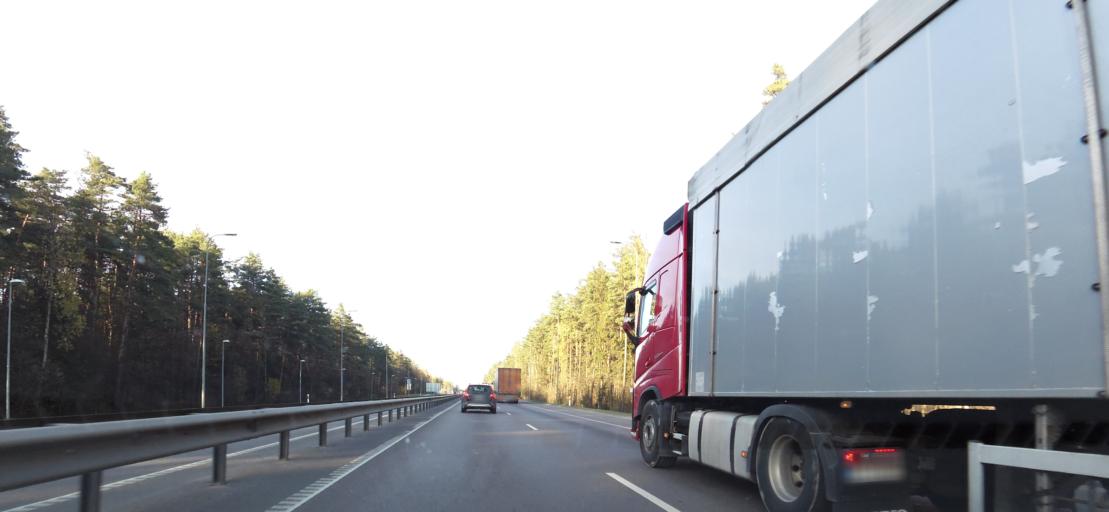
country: LT
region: Vilnius County
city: Lazdynai
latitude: 54.6461
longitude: 25.1510
